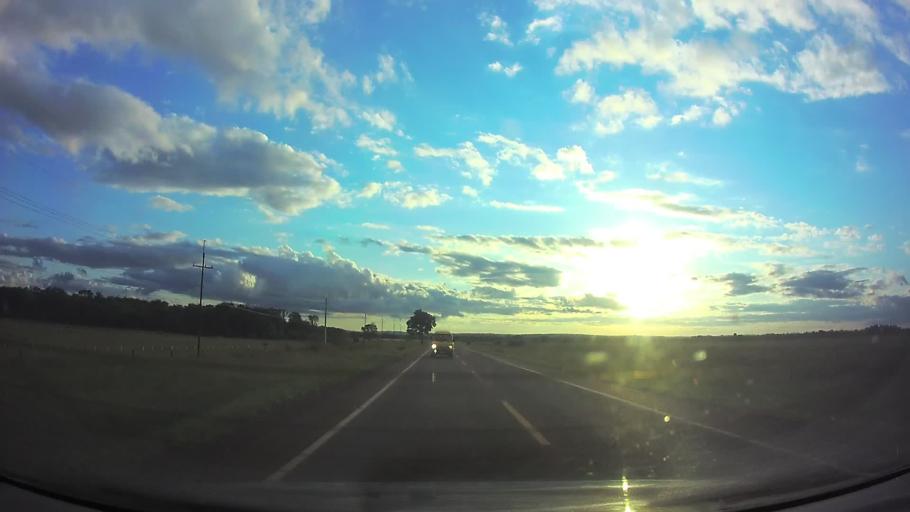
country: PY
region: Paraguari
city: Carapegua
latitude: -25.7154
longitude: -57.1950
